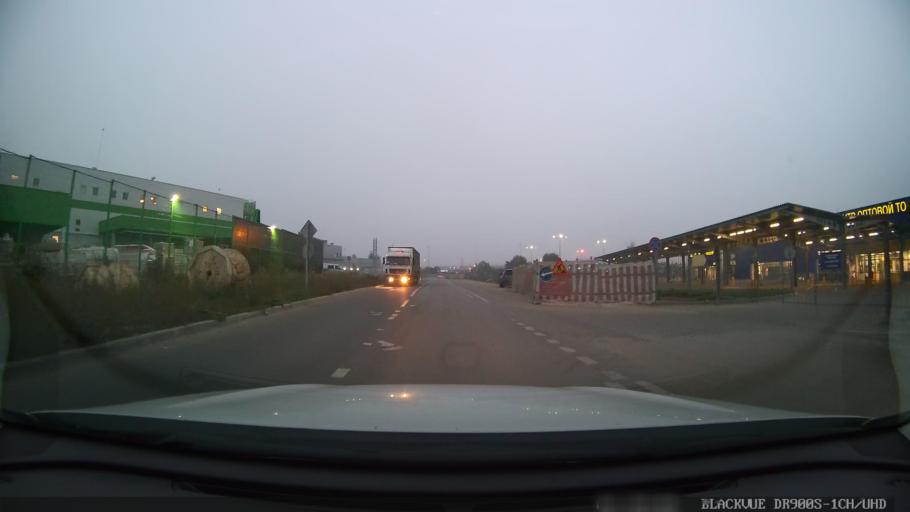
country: RU
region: Moscow
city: Solntsevo
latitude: 55.6199
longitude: 37.3898
